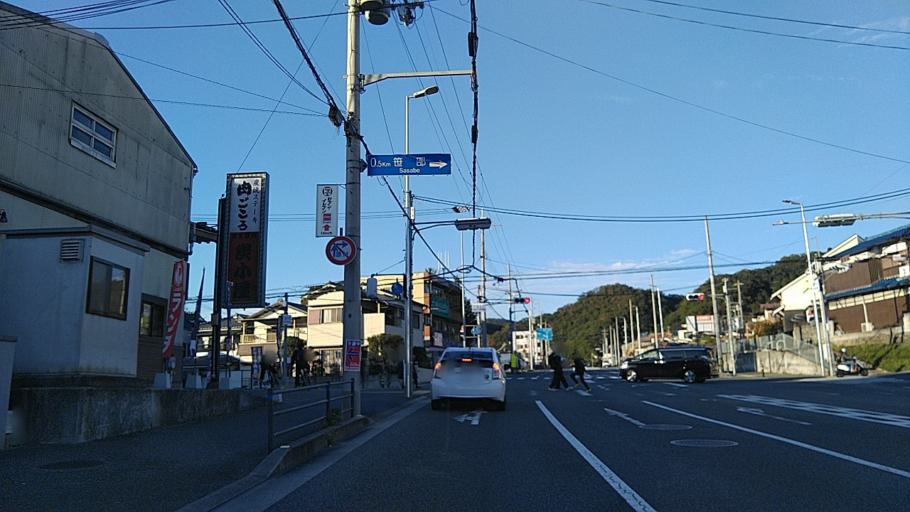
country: JP
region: Osaka
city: Ikeda
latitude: 34.8948
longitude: 135.4073
